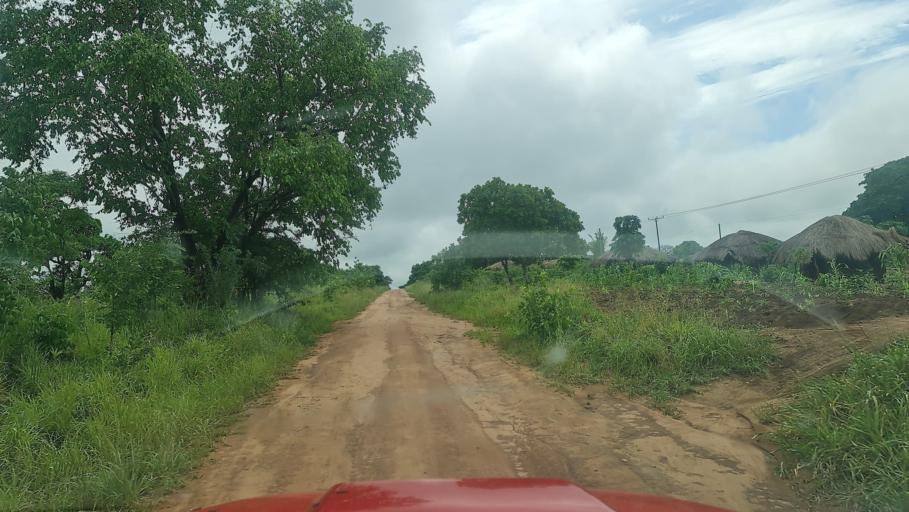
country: MW
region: Southern Region
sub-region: Nsanje District
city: Nsanje
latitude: -17.1857
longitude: 35.9202
